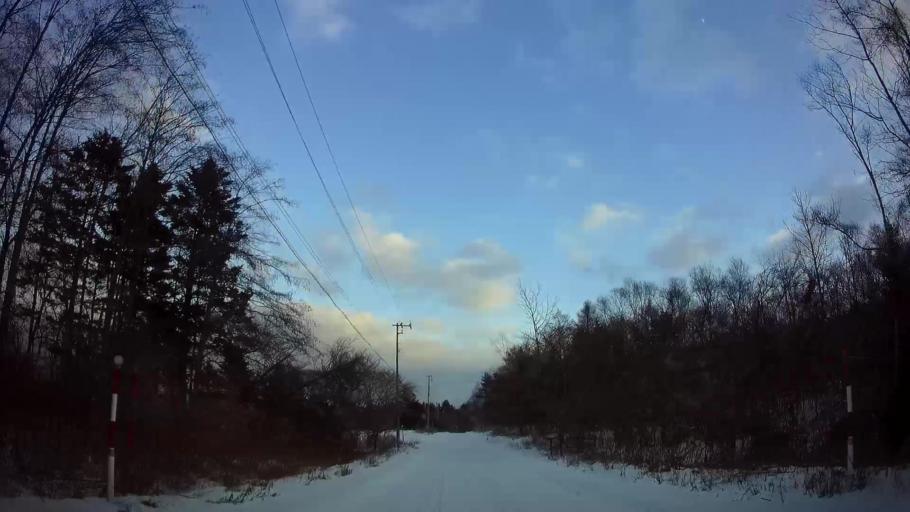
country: JP
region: Hokkaido
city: Nanae
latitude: 42.0198
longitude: 140.8413
